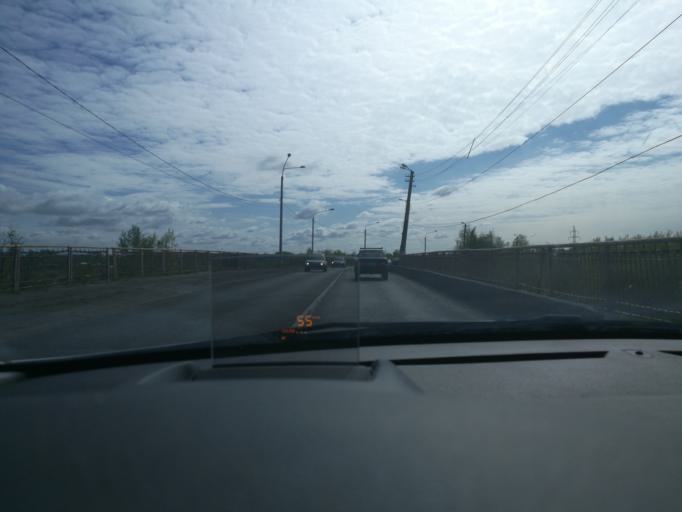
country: RU
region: Arkhangelskaya
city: Arkhangel'sk
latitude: 64.5998
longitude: 40.5526
